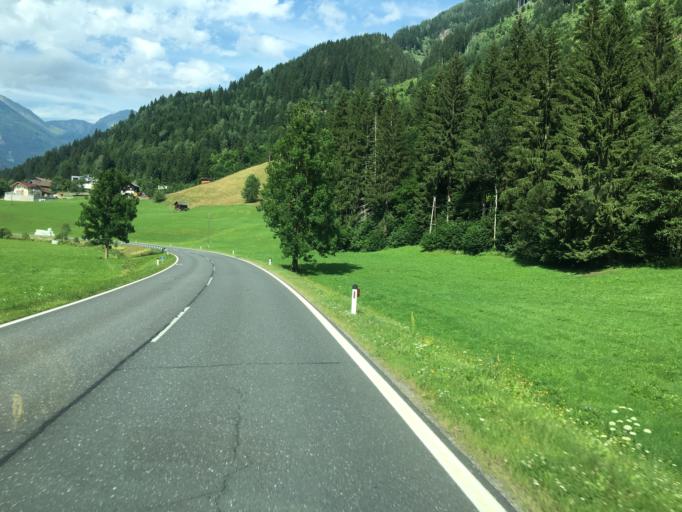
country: AT
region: Carinthia
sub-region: Politischer Bezirk Spittal an der Drau
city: Stall
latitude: 46.9005
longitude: 13.0677
